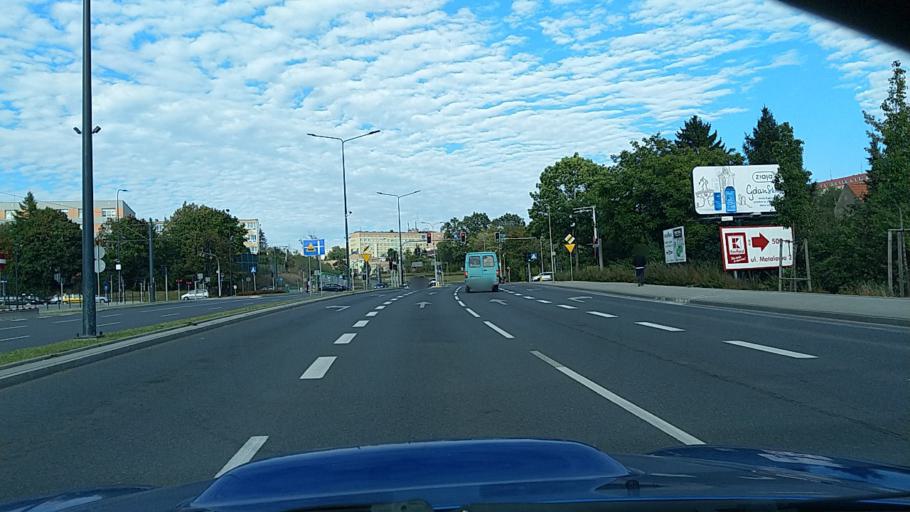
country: PL
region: Warmian-Masurian Voivodeship
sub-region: Powiat olsztynski
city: Olsztyn
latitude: 53.7656
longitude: 20.4868
